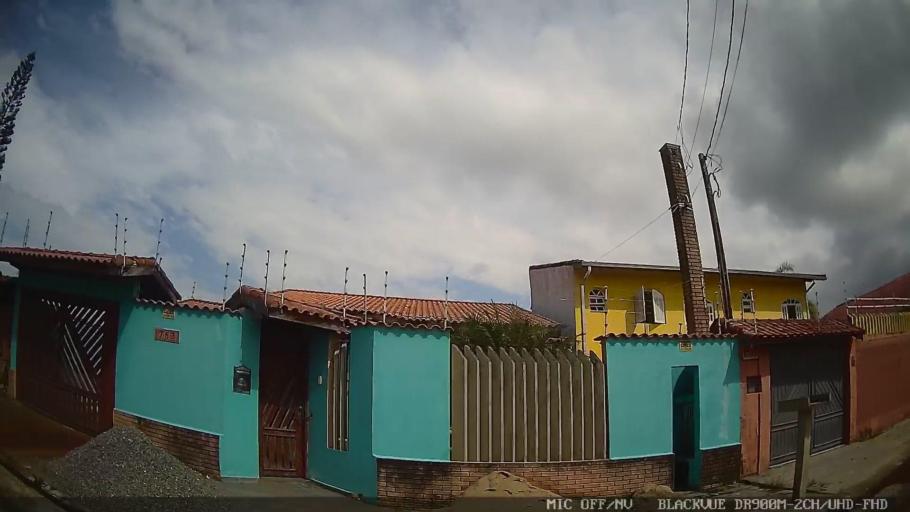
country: BR
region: Sao Paulo
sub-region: Itanhaem
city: Itanhaem
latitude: -24.1998
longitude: -46.8382
